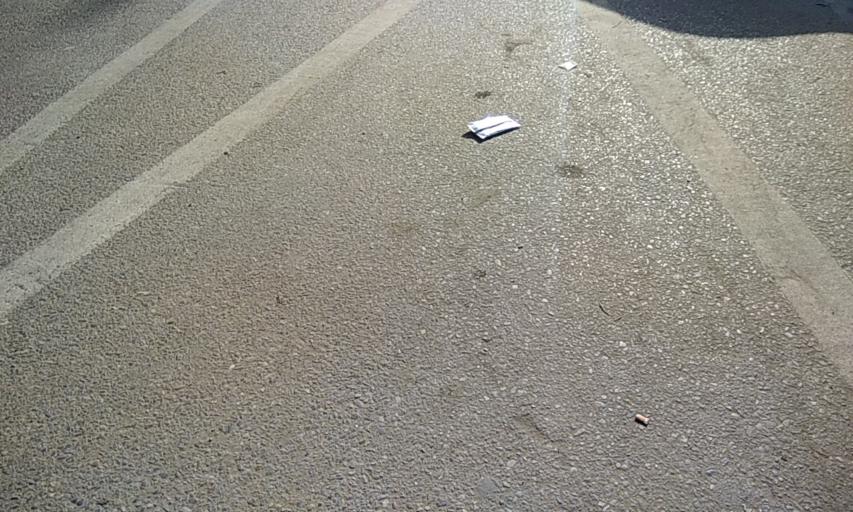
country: IN
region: Himachal Pradesh
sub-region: Kangra
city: Palampur
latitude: 32.0838
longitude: 76.5160
